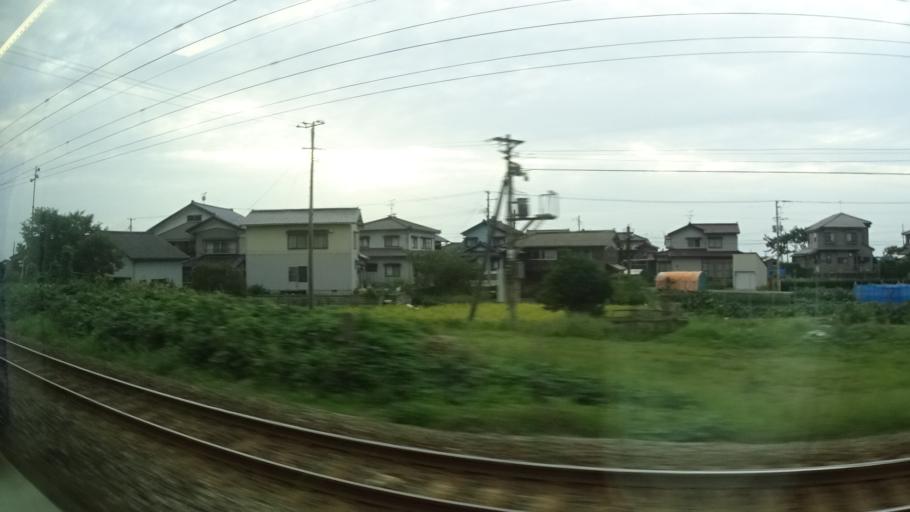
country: JP
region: Niigata
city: Murakami
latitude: 38.2700
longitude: 139.4491
